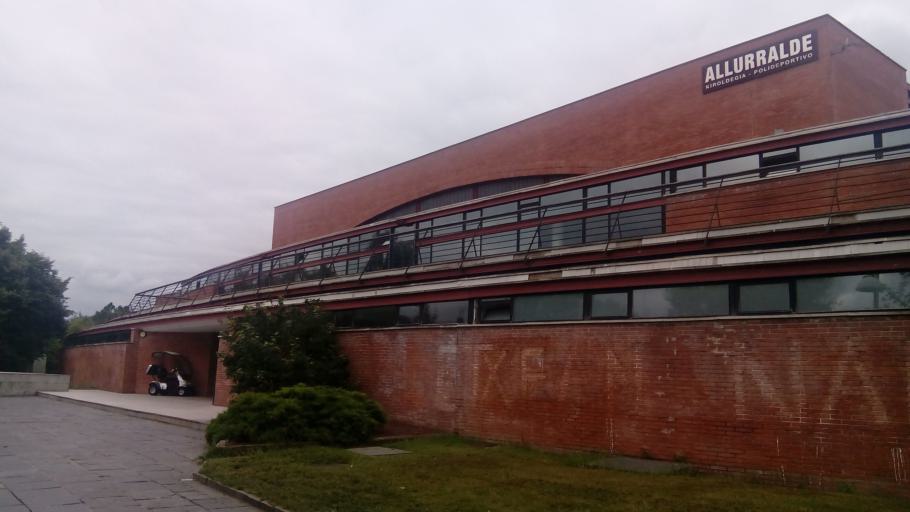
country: ES
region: Basque Country
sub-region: Provincia de Guipuzcoa
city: Andoain
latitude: 43.2151
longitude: -2.0220
